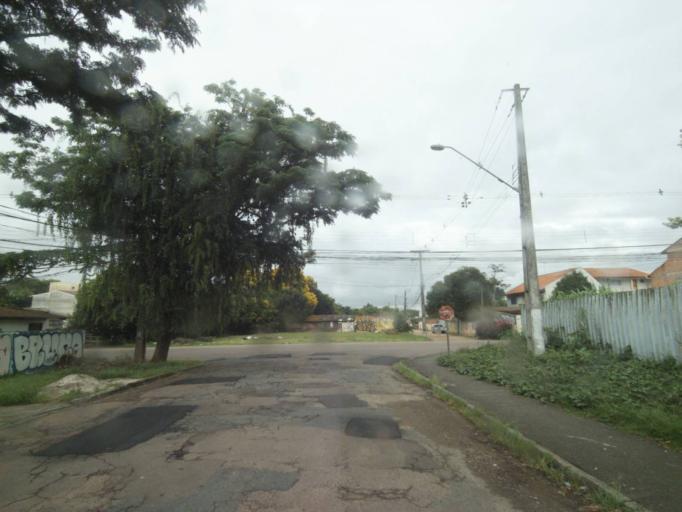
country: BR
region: Parana
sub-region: Curitiba
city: Curitiba
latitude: -25.4863
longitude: -49.3050
